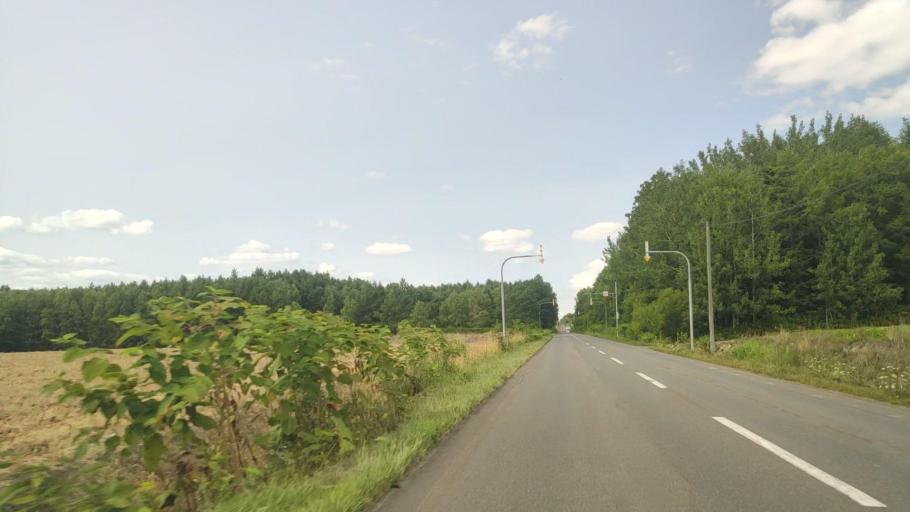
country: JP
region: Hokkaido
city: Nayoro
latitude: 44.2418
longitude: 142.4157
